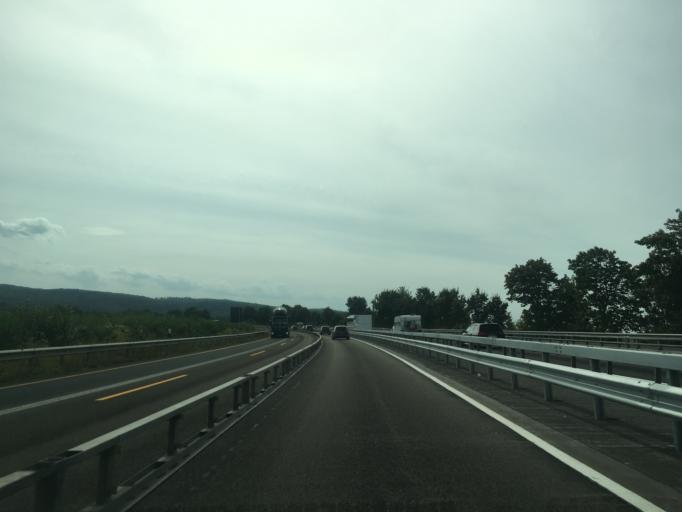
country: DE
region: Rheinland-Pfalz
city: Dieblich
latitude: 50.3082
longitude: 7.4858
